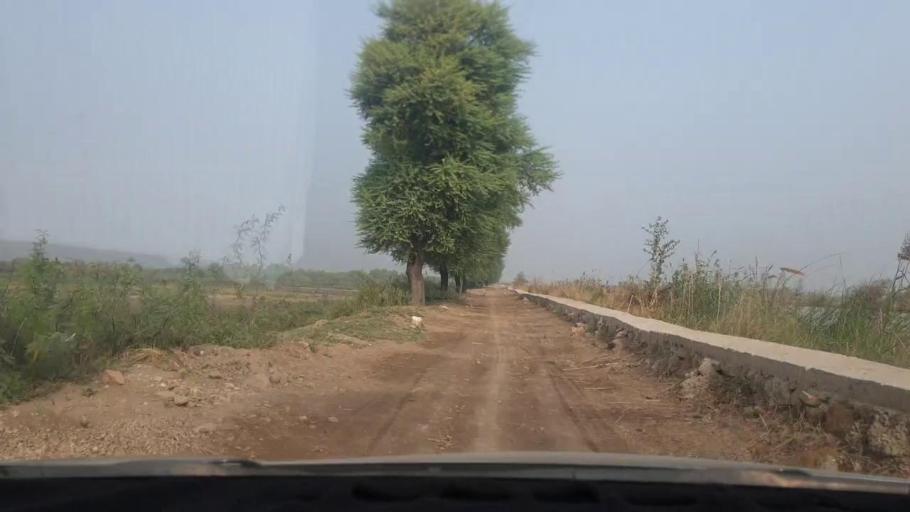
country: PK
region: Sindh
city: Matiari
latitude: 25.6641
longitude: 68.5595
